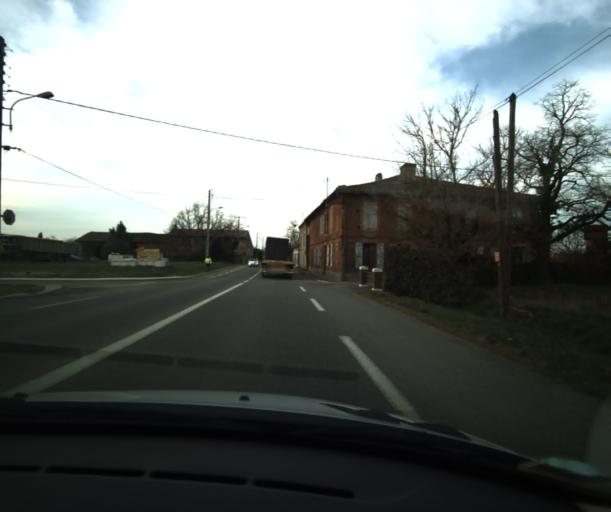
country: FR
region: Midi-Pyrenees
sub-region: Departement du Tarn-et-Garonne
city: Saint-Porquier
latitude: 44.0011
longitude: 1.1829
